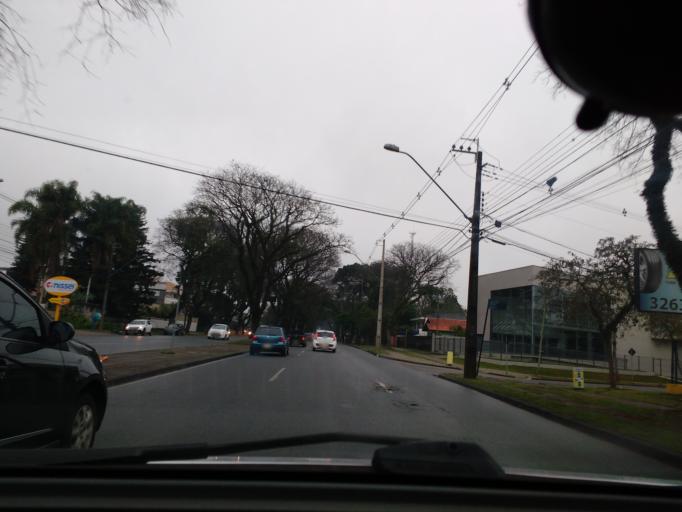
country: BR
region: Parana
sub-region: Curitiba
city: Curitiba
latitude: -25.4278
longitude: -49.2345
